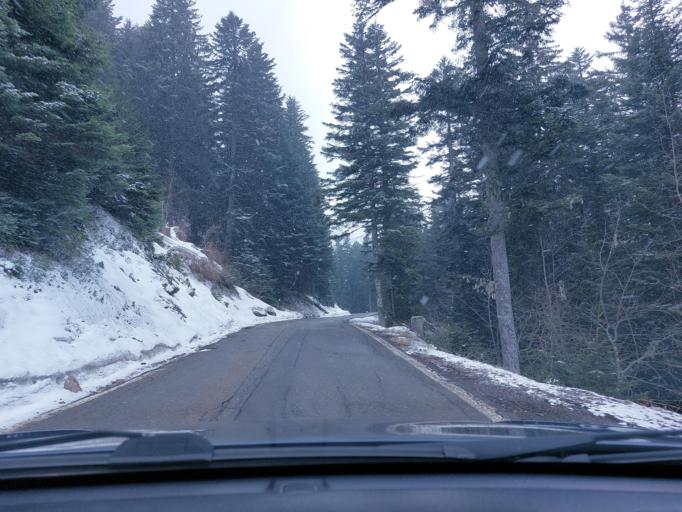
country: CH
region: Valais
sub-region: Sion District
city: Saviese
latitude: 46.2982
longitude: 7.3241
